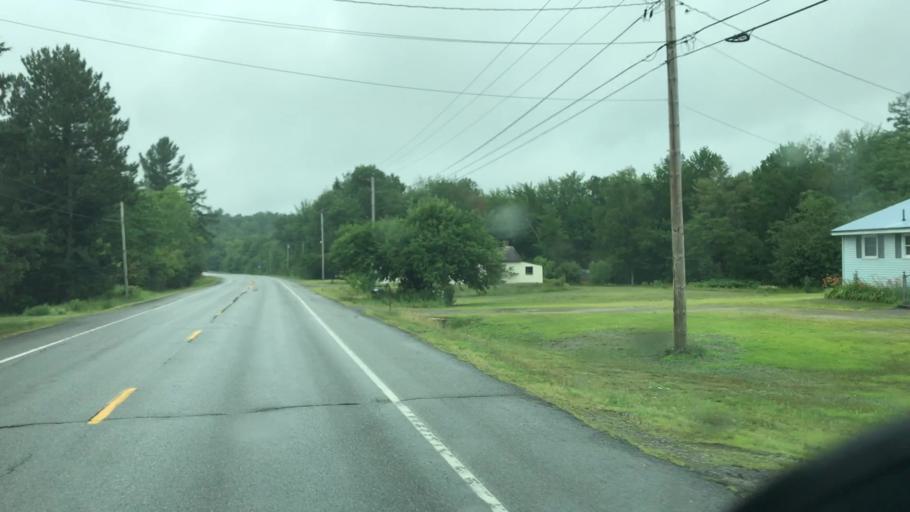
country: US
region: Maine
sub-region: Penobscot County
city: Lincoln
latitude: 45.3417
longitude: -68.5664
